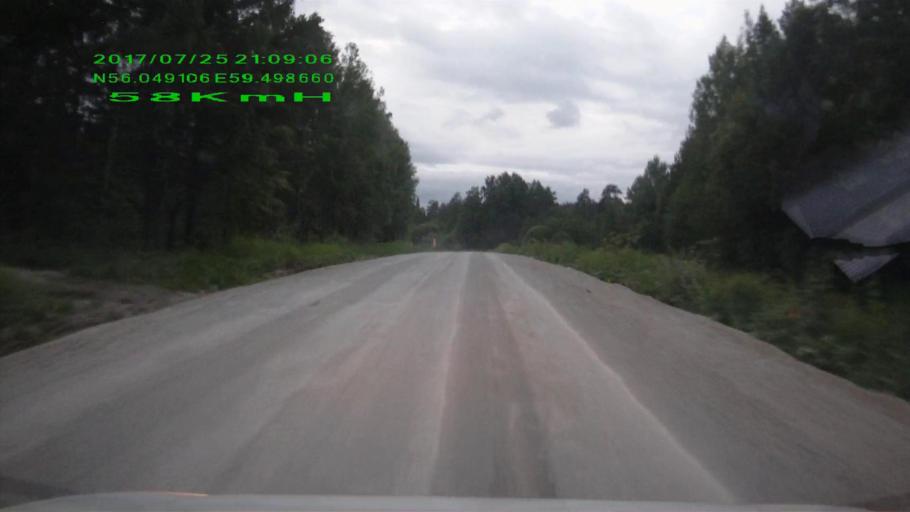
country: RU
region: Chelyabinsk
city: Nyazepetrovsk
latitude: 56.0493
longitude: 59.4981
